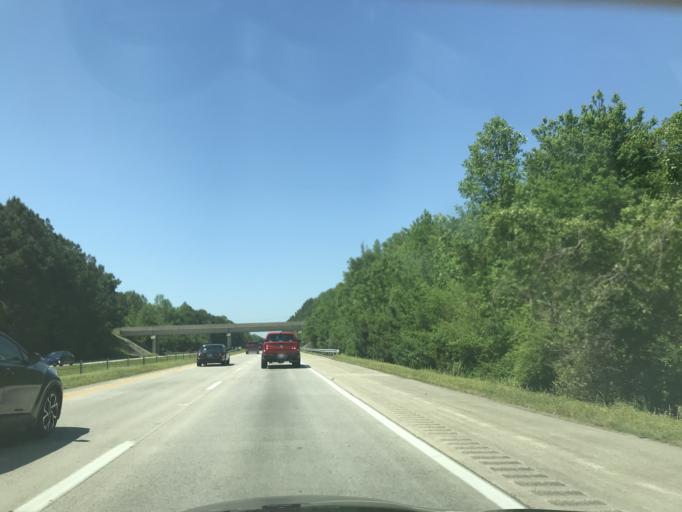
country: US
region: North Carolina
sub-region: Johnston County
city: Benson
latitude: 35.4891
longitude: -78.5521
